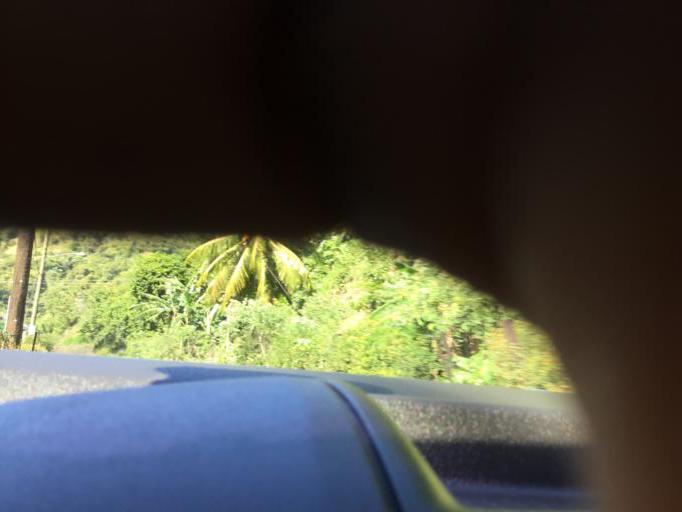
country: VC
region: Saint David
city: Chateaubelair
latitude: 13.2594
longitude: -61.2496
